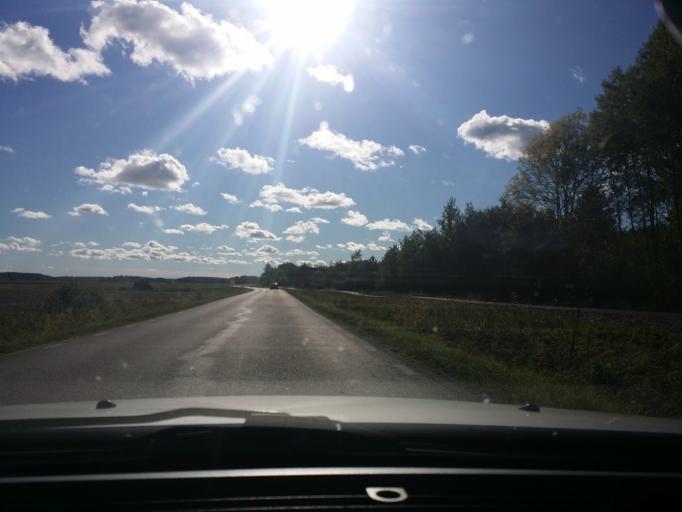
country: SE
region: Vaestmanland
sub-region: Vasteras
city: Vasteras
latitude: 59.5648
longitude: 16.4795
